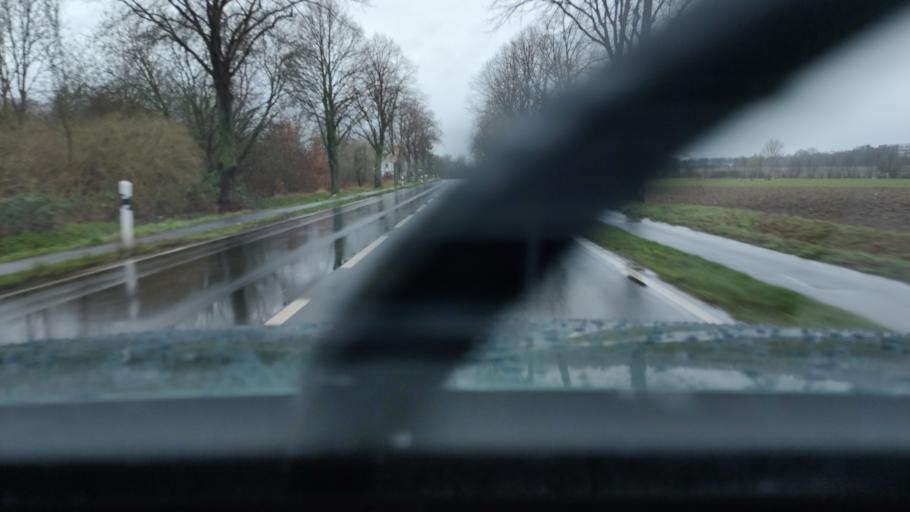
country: DE
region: Lower Saxony
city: Peine
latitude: 52.2945
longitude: 10.2323
